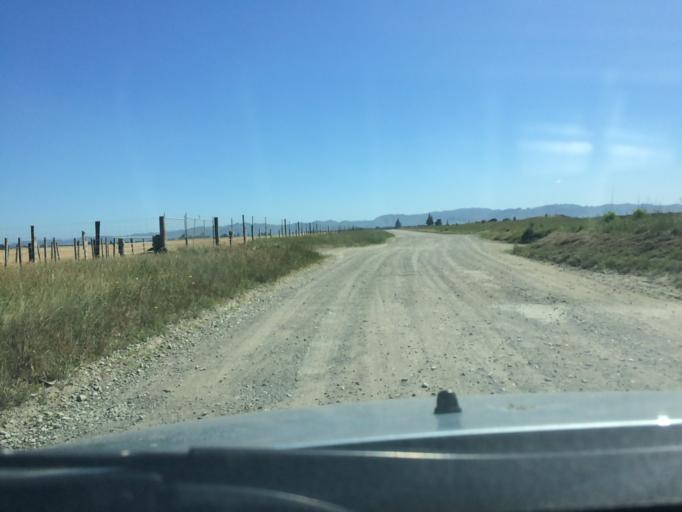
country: NZ
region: Gisborne
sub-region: Gisborne District
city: Gisborne
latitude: -38.7030
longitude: 177.9470
